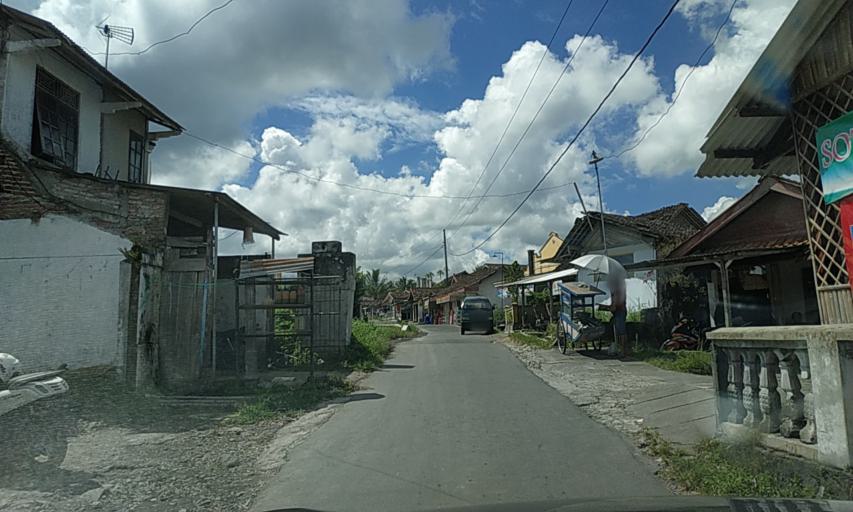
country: ID
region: Central Java
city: Muntilan
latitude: -7.5414
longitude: 110.3362
